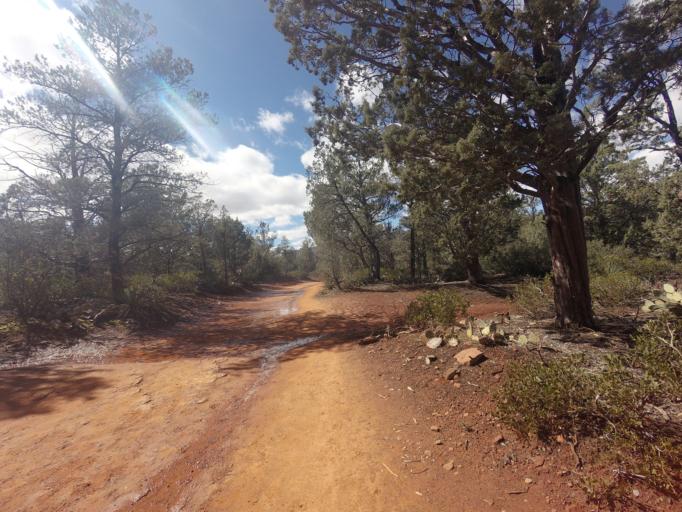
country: US
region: Arizona
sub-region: Yavapai County
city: West Sedona
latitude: 34.9017
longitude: -111.8118
